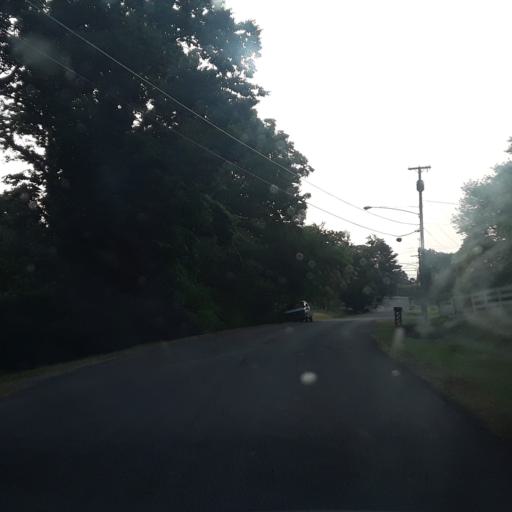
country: US
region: Tennessee
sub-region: Davidson County
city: Oak Hill
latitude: 36.0620
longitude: -86.7292
